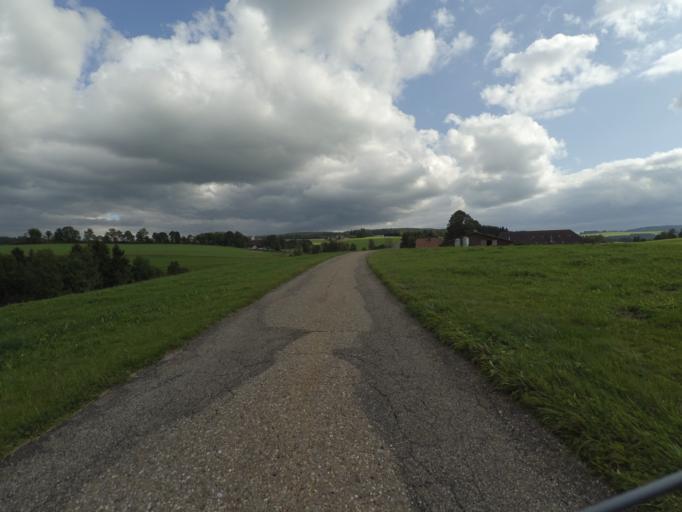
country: DE
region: Baden-Wuerttemberg
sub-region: Freiburg Region
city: Sankt Margen
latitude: 47.9815
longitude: 8.1016
